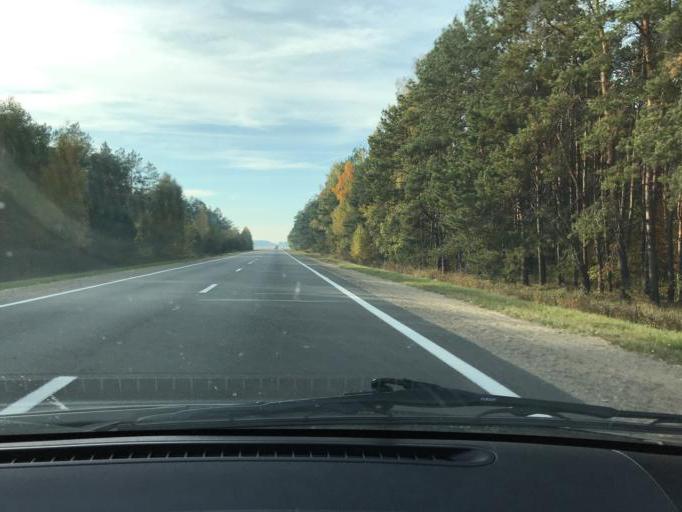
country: BY
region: Brest
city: Horad Pinsk
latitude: 52.1485
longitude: 25.8876
